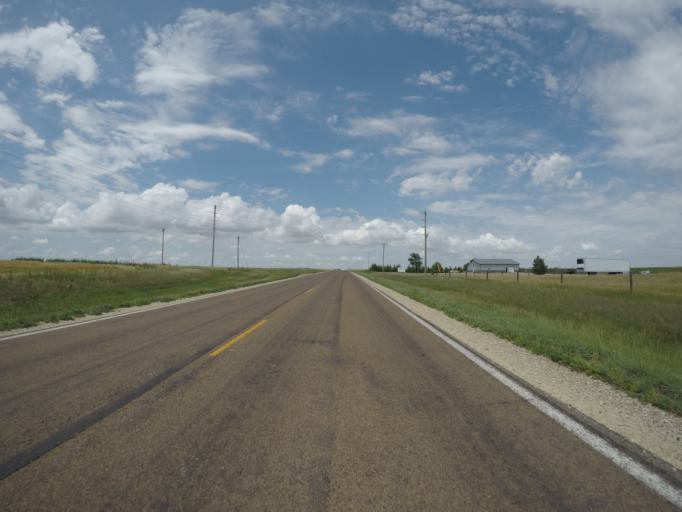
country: US
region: Kansas
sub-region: Rawlins County
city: Atwood
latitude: 39.8423
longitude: -101.0467
